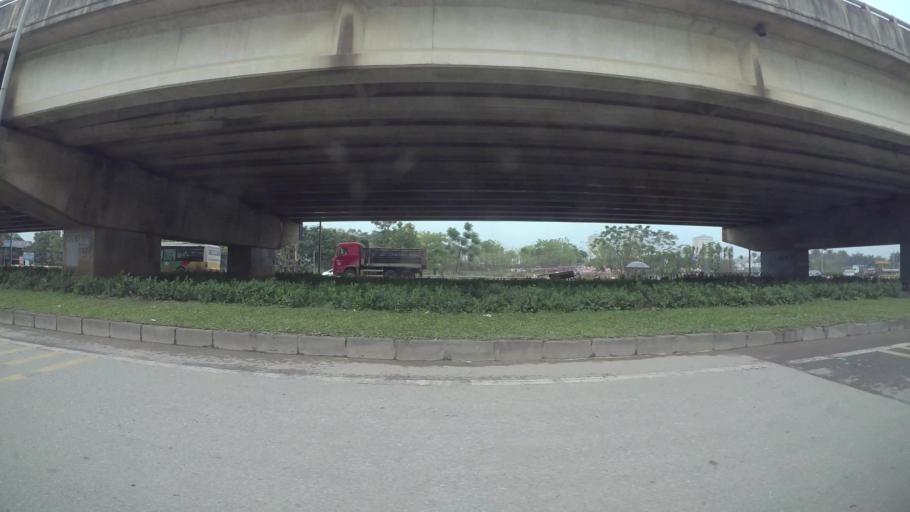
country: VN
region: Ha Noi
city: Tay Ho
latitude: 21.1248
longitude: 105.7817
